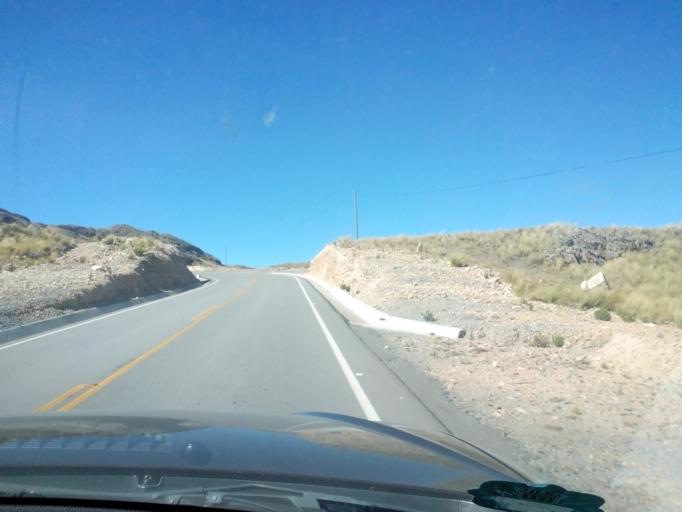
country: PE
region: Ayacucho
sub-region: Provincia de Huamanga
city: Acocro
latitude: -13.3631
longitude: -74.0834
